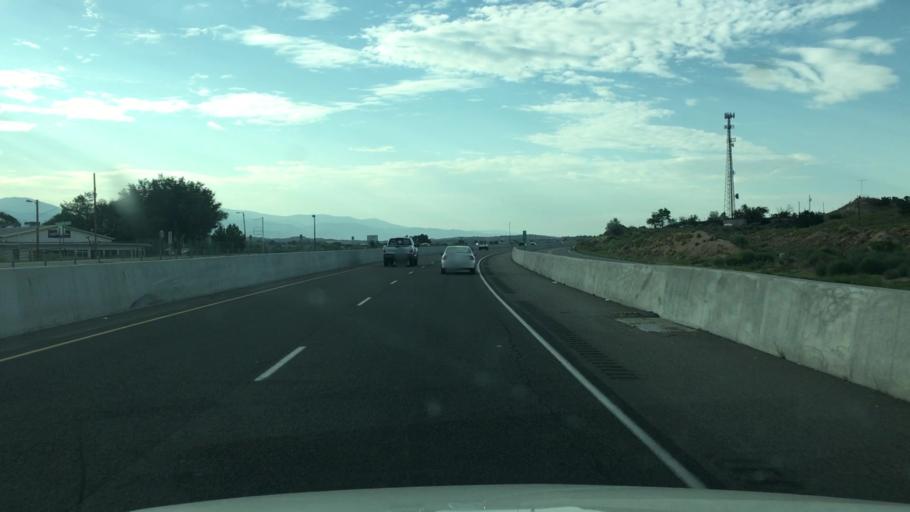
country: US
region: New Mexico
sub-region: Santa Fe County
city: El Valle de Arroyo Seco
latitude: 35.9575
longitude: -106.0234
